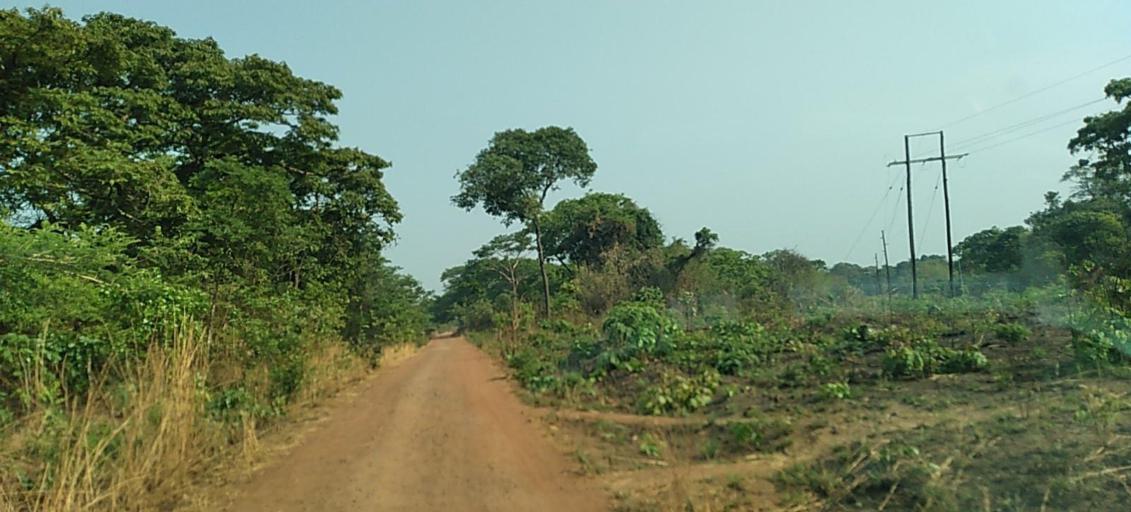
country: ZM
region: Copperbelt
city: Chingola
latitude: -12.8409
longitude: 27.5457
